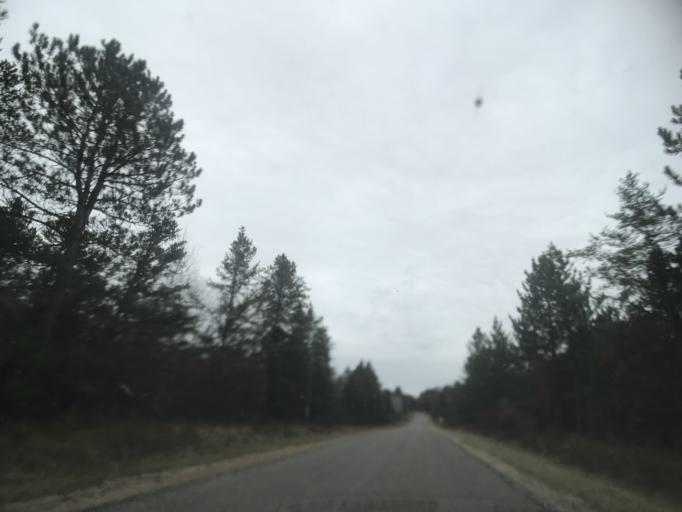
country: US
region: Wisconsin
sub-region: Oconto County
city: Gillett
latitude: 45.2750
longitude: -88.2571
